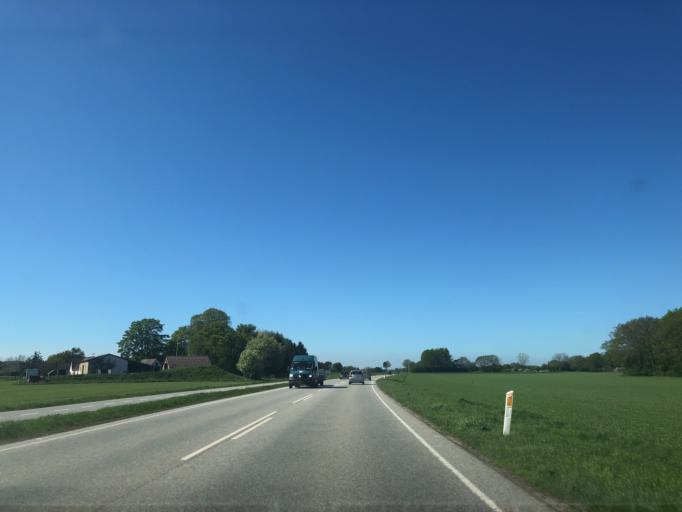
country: DK
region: Zealand
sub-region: Stevns Kommune
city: Store Heddinge
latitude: 55.3413
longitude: 12.3414
